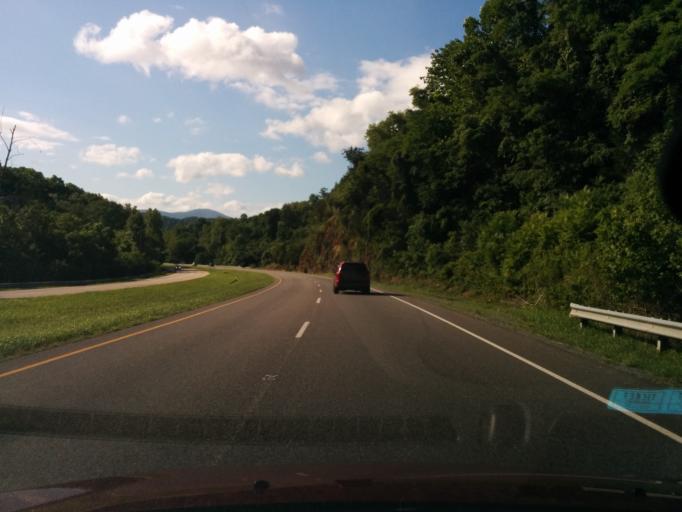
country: US
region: Virginia
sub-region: City of Lexington
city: Lexington
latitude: 37.7662
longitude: -79.4298
